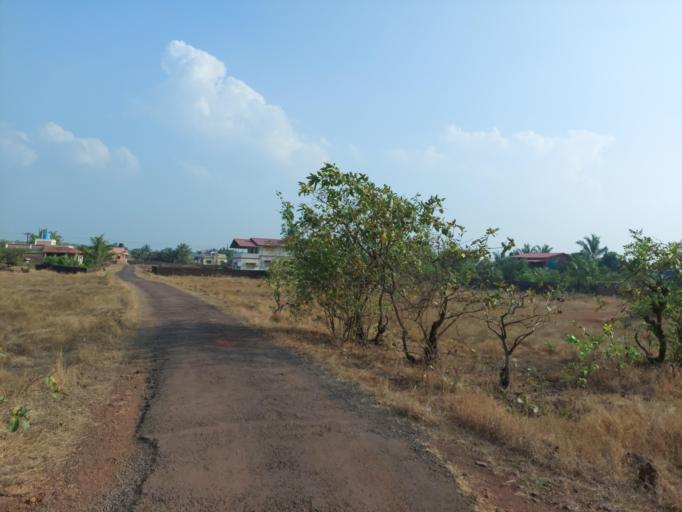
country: IN
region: Maharashtra
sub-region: Ratnagiri
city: Ratnagiri
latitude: 16.9352
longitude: 73.3248
